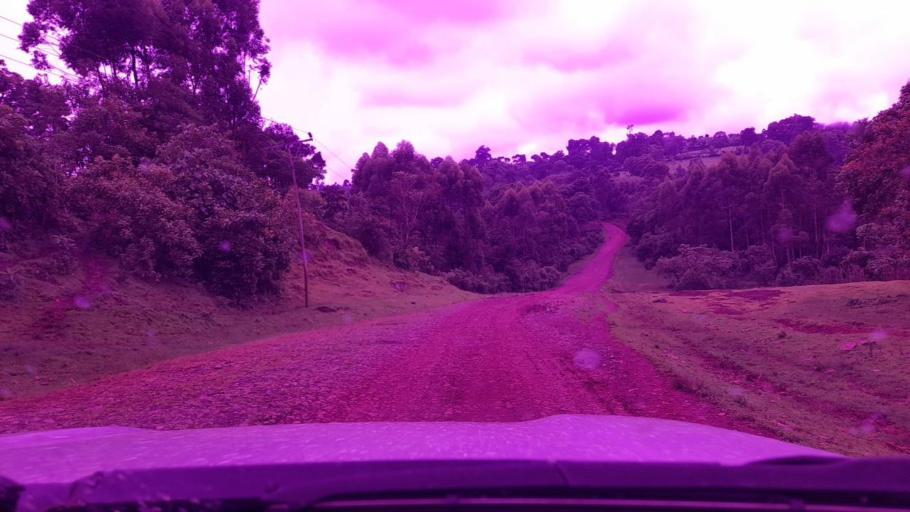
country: ET
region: Southern Nations, Nationalities, and People's Region
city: Tippi
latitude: 7.5757
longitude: 35.7801
